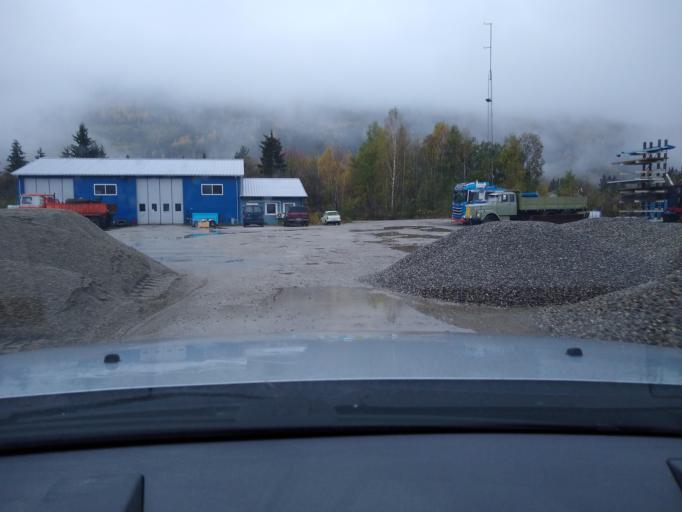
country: NO
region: Oppland
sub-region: Ringebu
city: Ringebu
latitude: 61.5432
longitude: 10.0574
